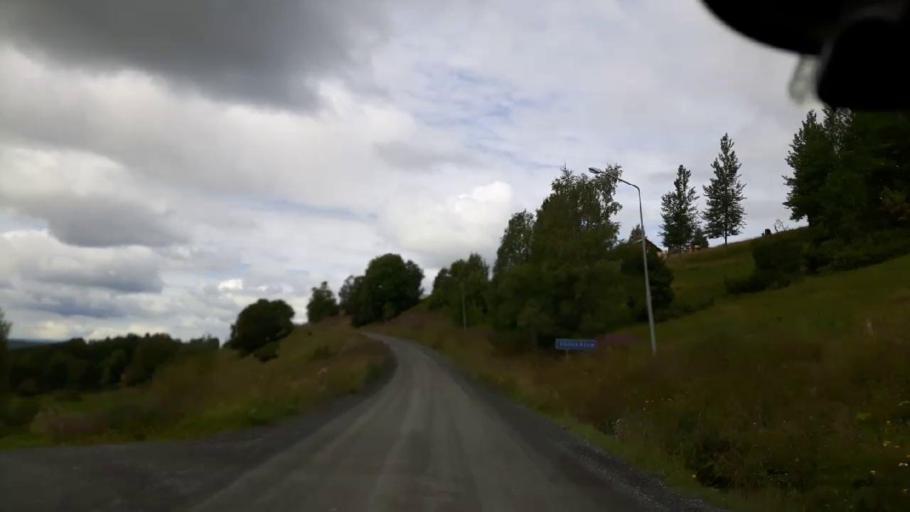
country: SE
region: Jaemtland
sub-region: Krokoms Kommun
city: Valla
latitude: 63.4997
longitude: 13.9683
